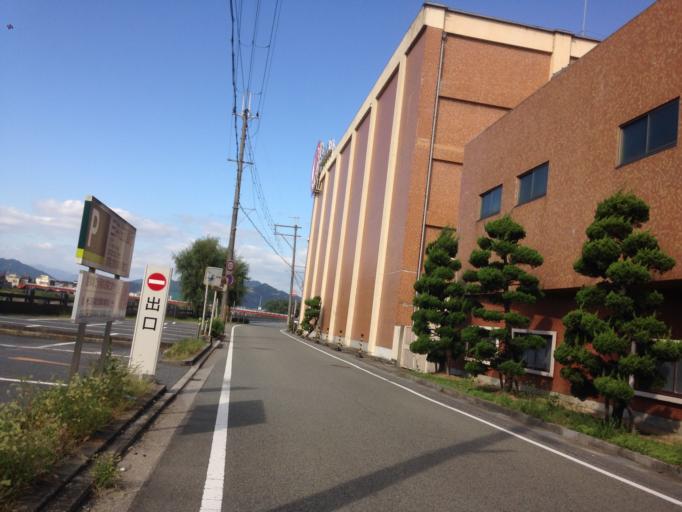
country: JP
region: Hyogo
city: Tatsunocho-tominaga
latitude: 34.8634
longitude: 134.5491
